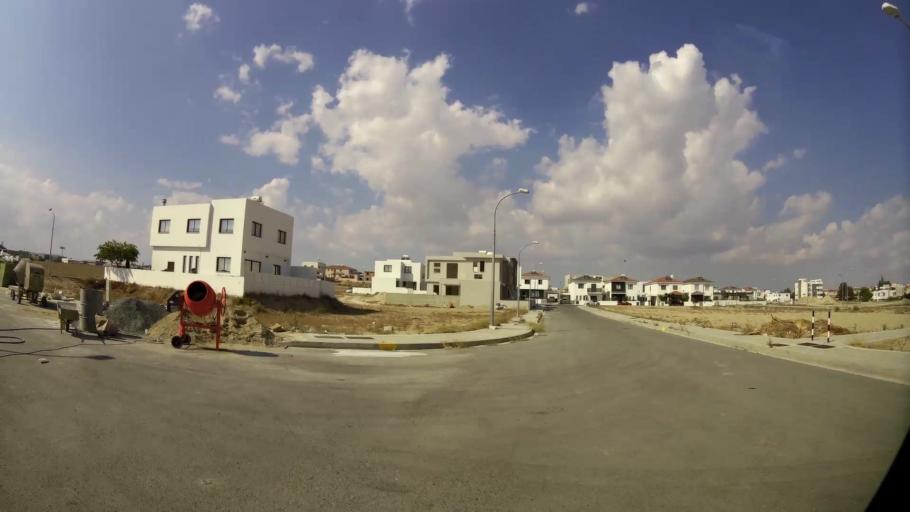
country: CY
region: Larnaka
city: Dhromolaxia
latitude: 34.9037
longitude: 33.5817
